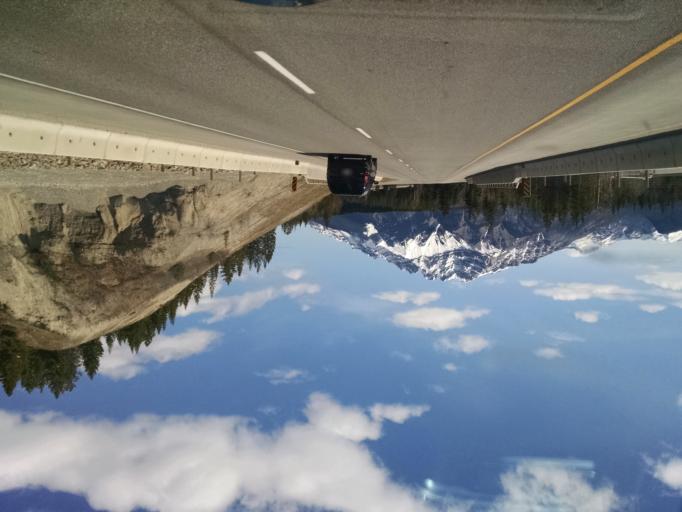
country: CA
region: Alberta
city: Canmore
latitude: 51.1495
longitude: -115.4278
